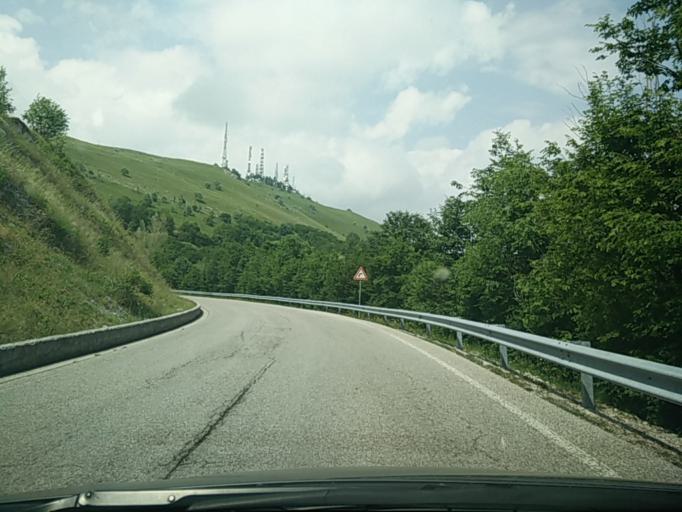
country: IT
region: Friuli Venezia Giulia
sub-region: Provincia di Pordenone
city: Budoia
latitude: 46.0823
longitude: 12.5306
